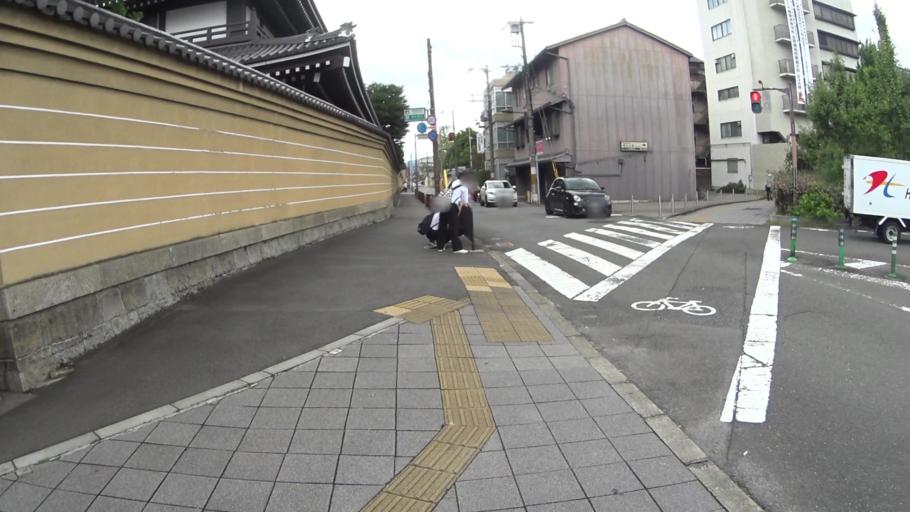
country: JP
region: Kyoto
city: Kyoto
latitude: 34.9927
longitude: 135.7527
